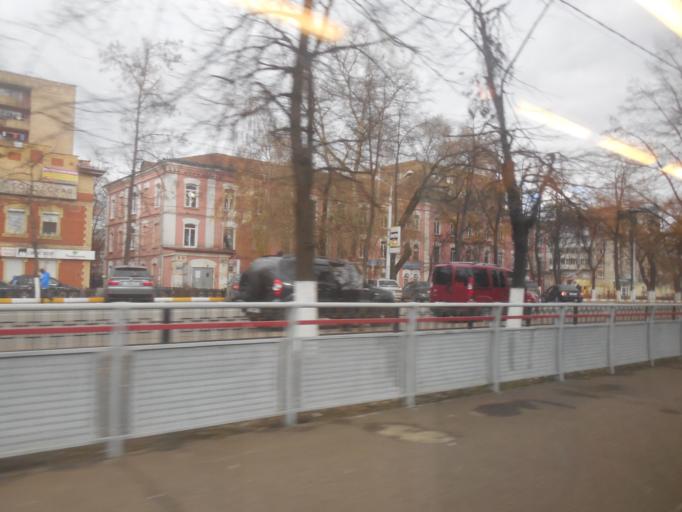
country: RU
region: Moskovskaya
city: Ramenskoye
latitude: 55.5718
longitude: 38.2098
